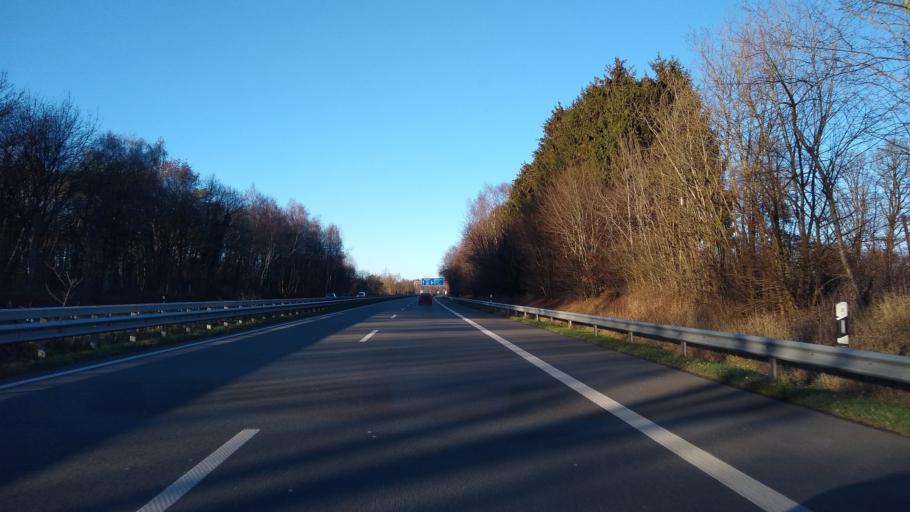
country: DE
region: Lower Saxony
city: Oldenburg
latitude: 53.1935
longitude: 8.2232
